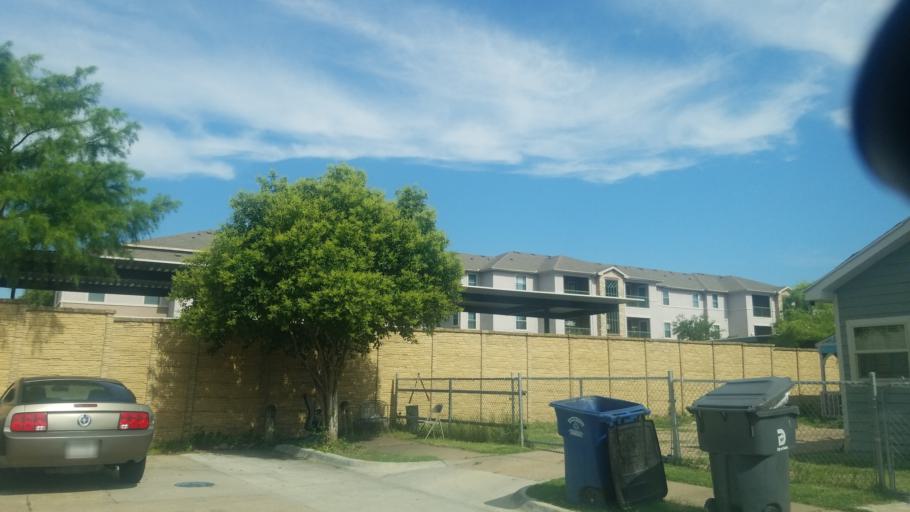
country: US
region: Texas
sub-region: Dallas County
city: Dallas
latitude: 32.7802
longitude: -96.8547
